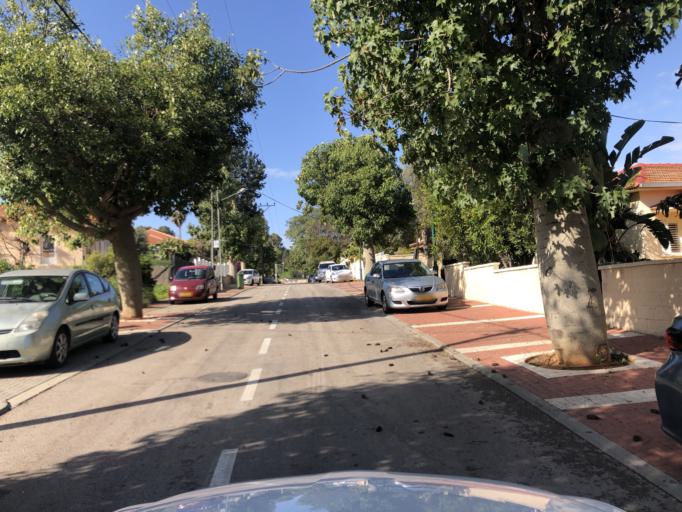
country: IL
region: Central District
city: Ness Ziona
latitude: 31.9166
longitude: 34.7960
